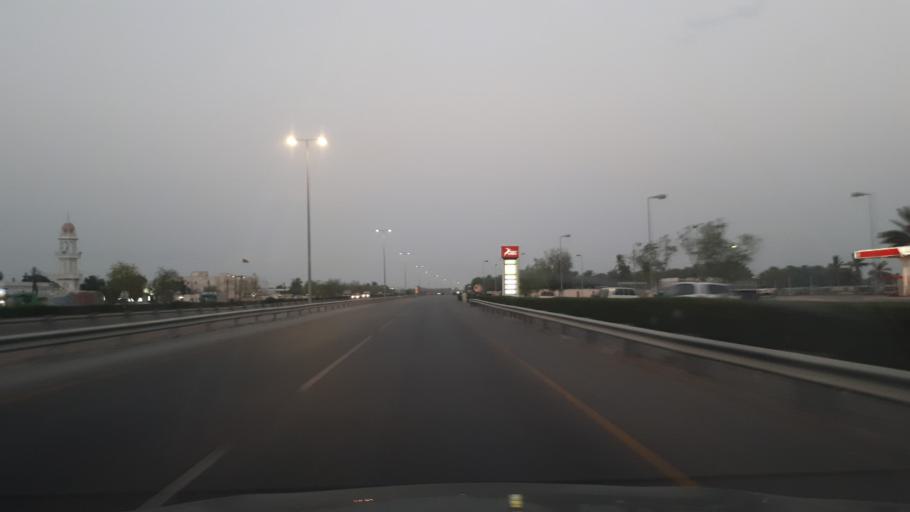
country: OM
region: Al Batinah
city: Barka'
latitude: 23.7351
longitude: 57.6769
